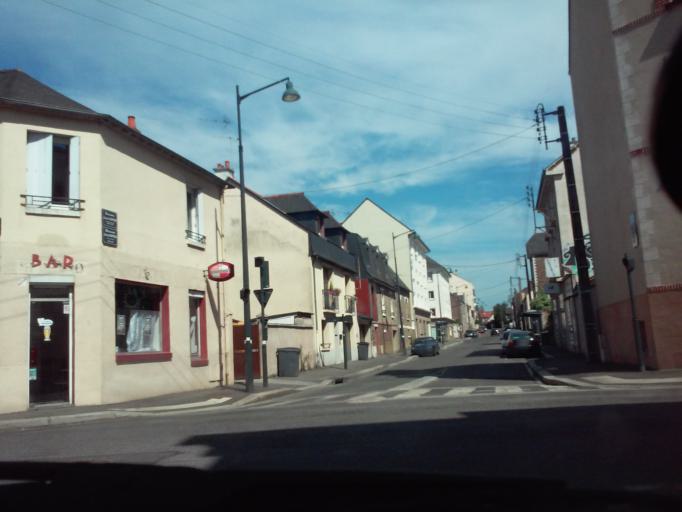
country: FR
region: Brittany
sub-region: Departement d'Ille-et-Vilaine
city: Rennes
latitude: 48.0978
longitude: -1.6721
